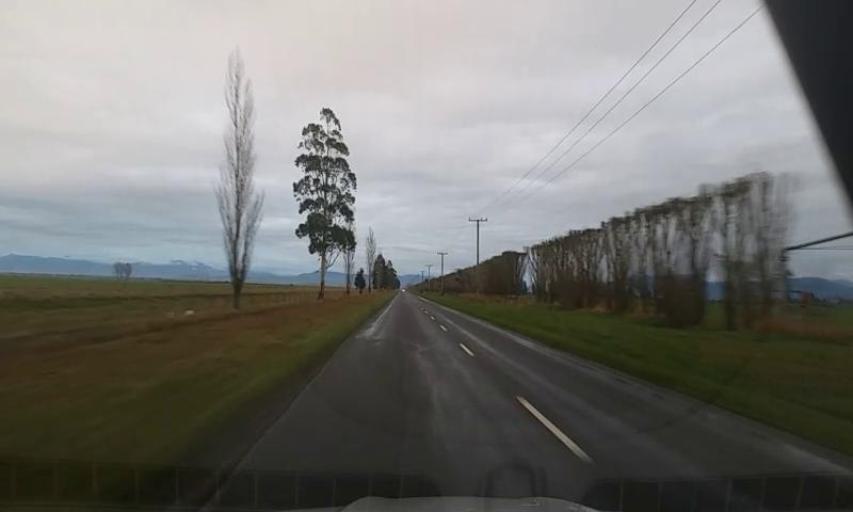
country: NZ
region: Canterbury
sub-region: Ashburton District
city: Methven
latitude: -43.7400
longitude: 171.6876
